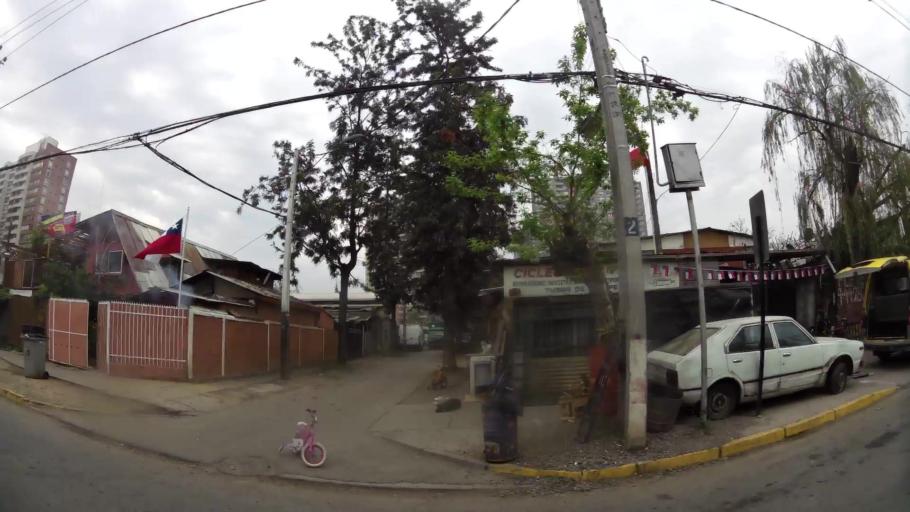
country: CL
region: Santiago Metropolitan
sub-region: Provincia de Santiago
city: Villa Presidente Frei, Nunoa, Santiago, Chile
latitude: -33.5060
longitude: -70.5924
